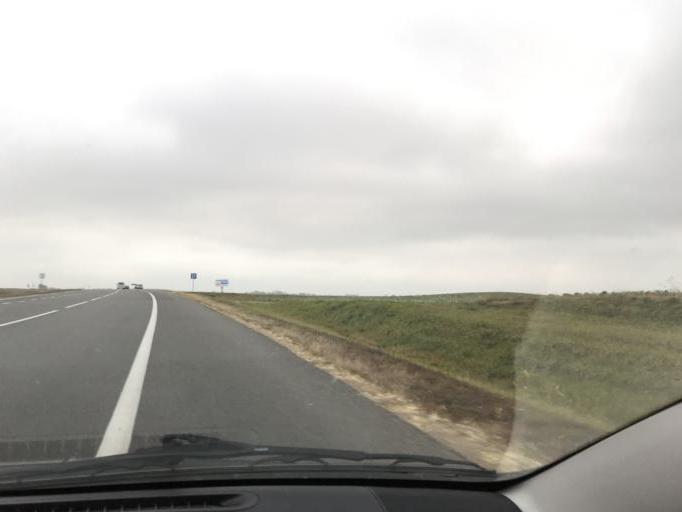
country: BY
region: Vitebsk
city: Vitebsk
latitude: 55.1609
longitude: 30.0663
